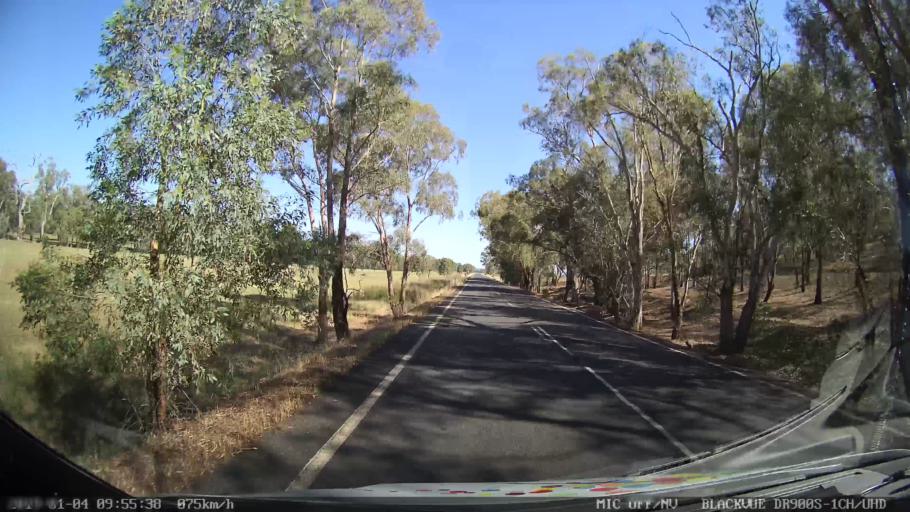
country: AU
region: New South Wales
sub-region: Cabonne
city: Canowindra
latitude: -33.5329
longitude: 148.4028
